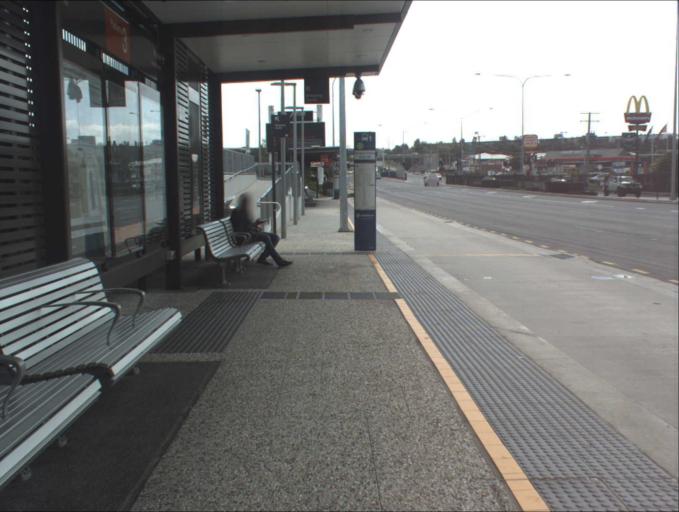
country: AU
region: Queensland
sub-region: Brisbane
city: Sunnybank Hills
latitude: -27.6611
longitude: 153.0416
